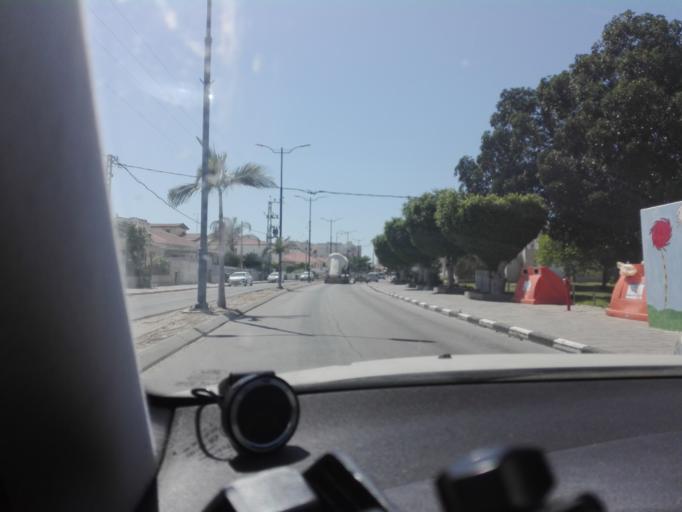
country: IL
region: Central District
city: Bene 'Ayish
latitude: 31.7298
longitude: 34.7431
